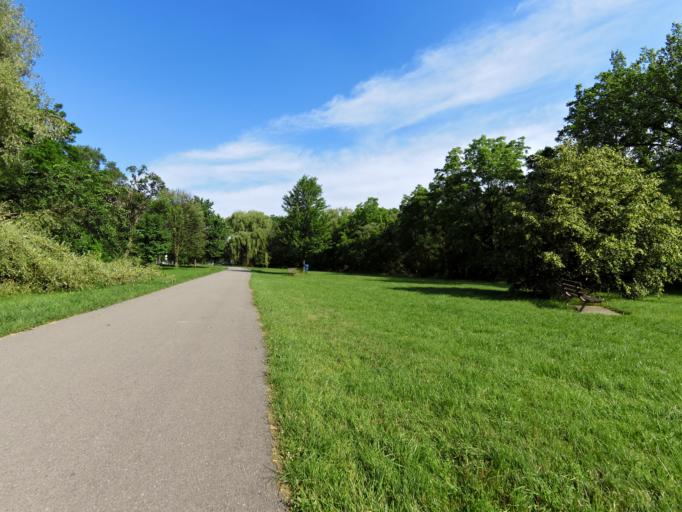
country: CA
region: Ontario
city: Etobicoke
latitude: 43.7031
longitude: -79.5283
